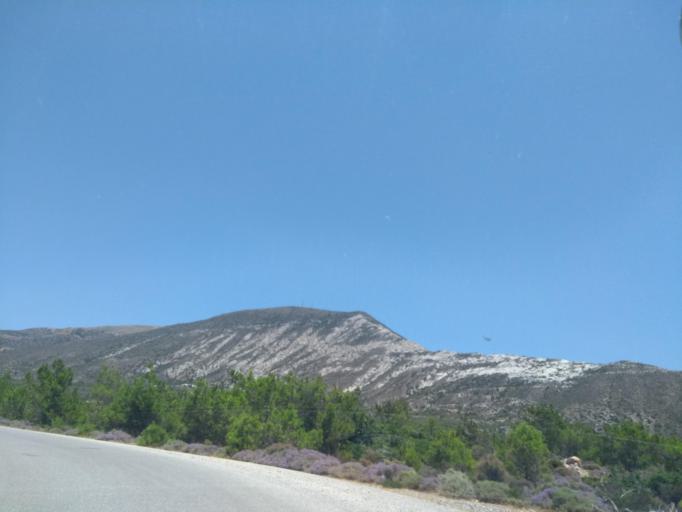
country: GR
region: Crete
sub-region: Nomos Chanias
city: Vryses
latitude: 35.3318
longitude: 23.5447
